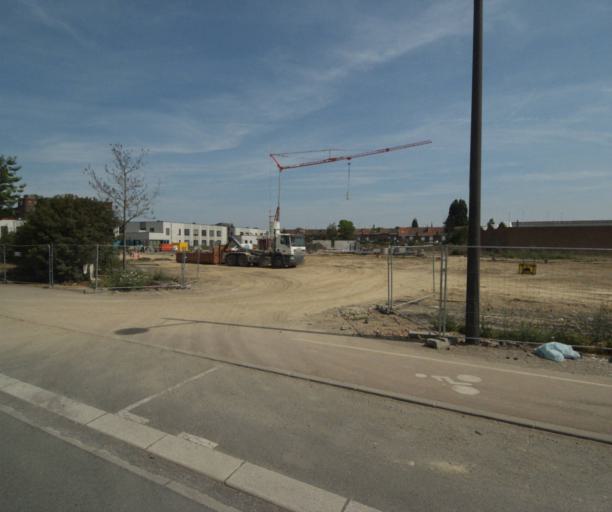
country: FR
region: Nord-Pas-de-Calais
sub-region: Departement du Nord
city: Tourcoing
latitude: 50.7121
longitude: 3.1477
